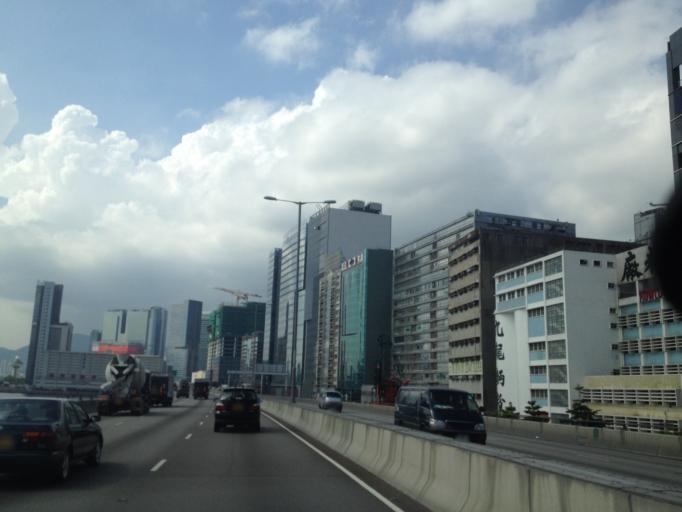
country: HK
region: Kowloon City
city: Kowloon
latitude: 22.3101
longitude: 114.2191
